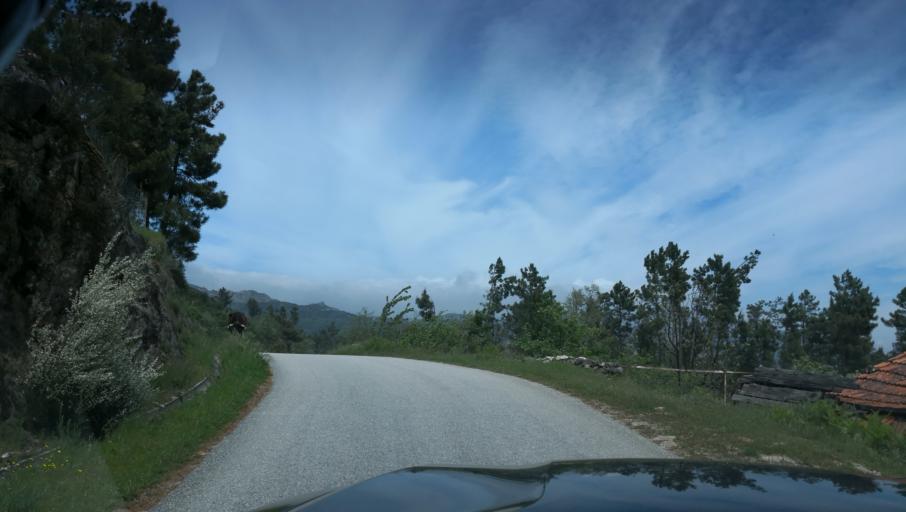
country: PT
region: Vila Real
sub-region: Vila Real
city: Vila Real
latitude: 41.3003
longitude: -7.8033
